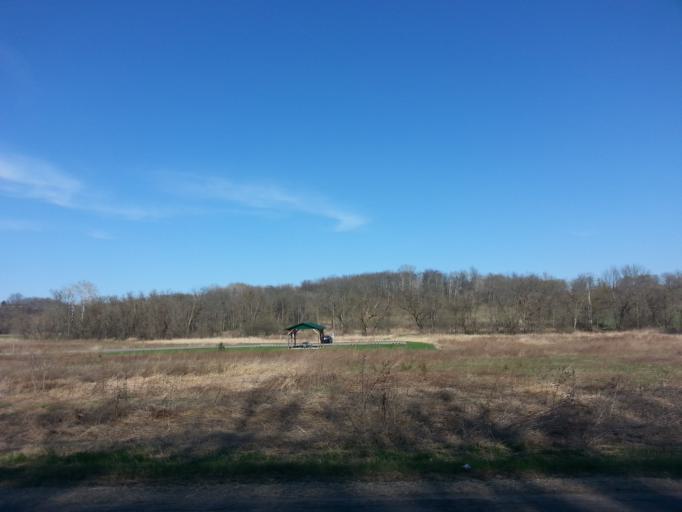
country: US
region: Wisconsin
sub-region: Pierce County
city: Ellsworth
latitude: 44.7252
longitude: -92.5805
